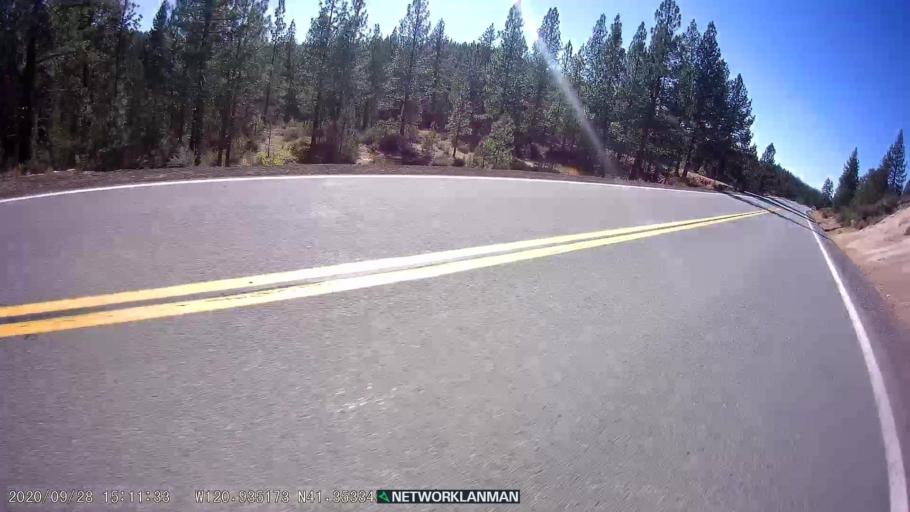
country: US
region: California
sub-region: Modoc County
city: Alturas
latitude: 41.3535
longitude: -120.9357
